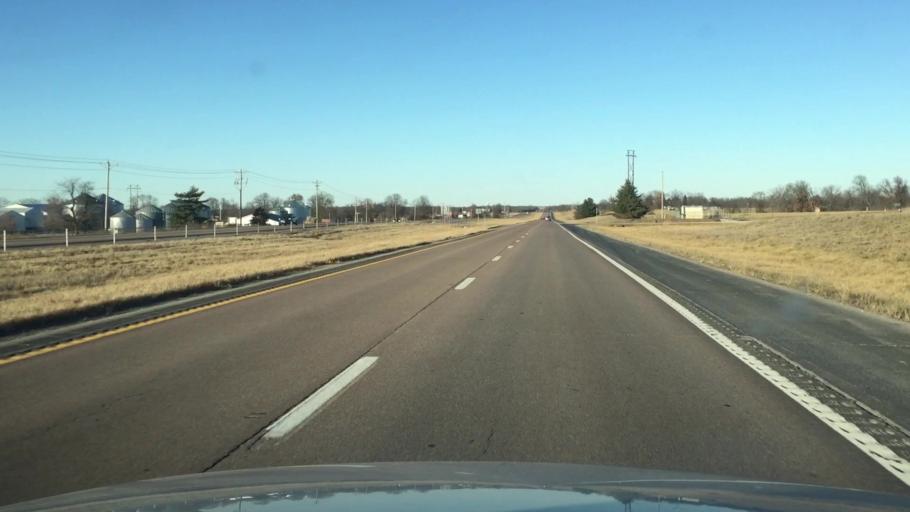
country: US
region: Missouri
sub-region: Boone County
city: Ashland
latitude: 38.7874
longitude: -92.2519
